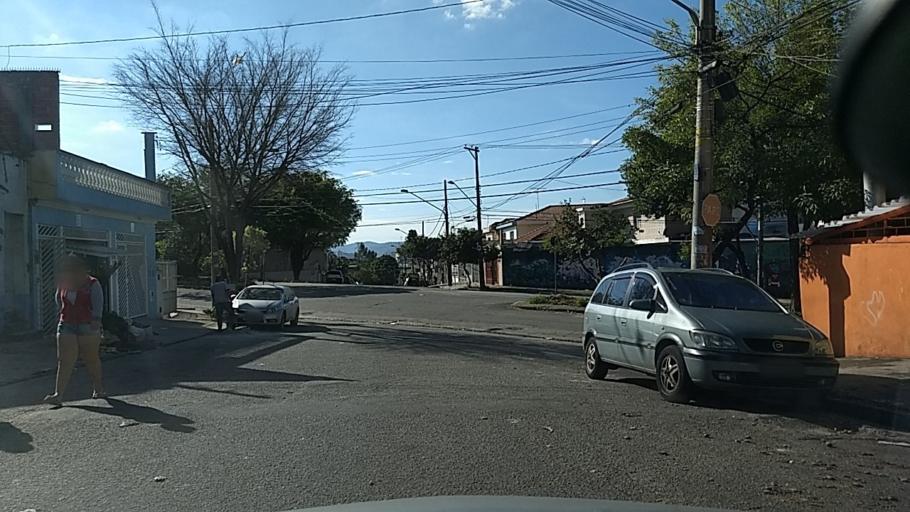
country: BR
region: Sao Paulo
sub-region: Guarulhos
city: Guarulhos
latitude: -23.5036
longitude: -46.5700
